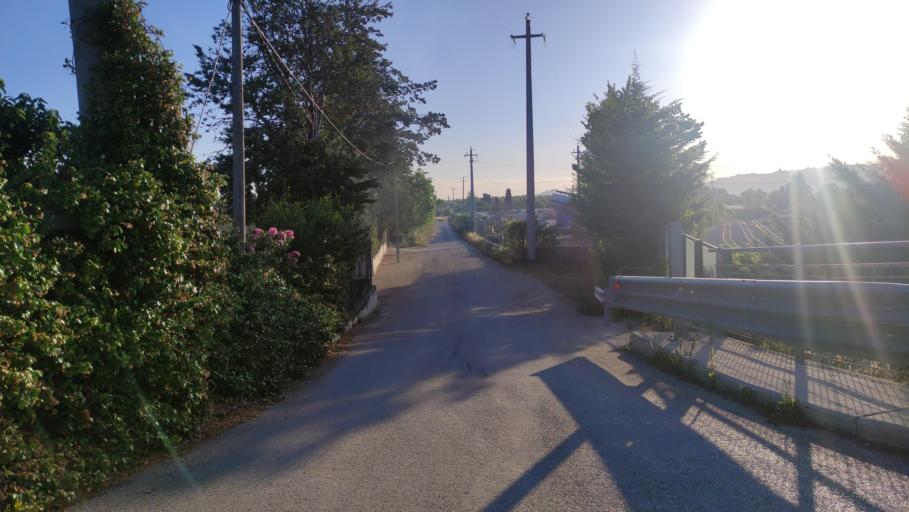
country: IT
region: Abruzzo
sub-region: Provincia di Pescara
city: Manoppello Scalo
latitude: 42.3258
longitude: 14.0835
